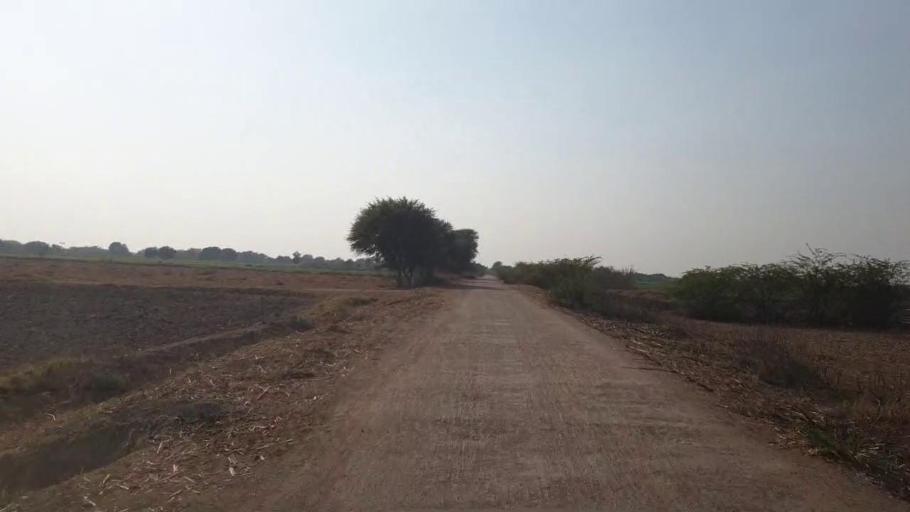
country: PK
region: Sindh
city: Mirpur Khas
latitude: 25.4130
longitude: 68.9395
